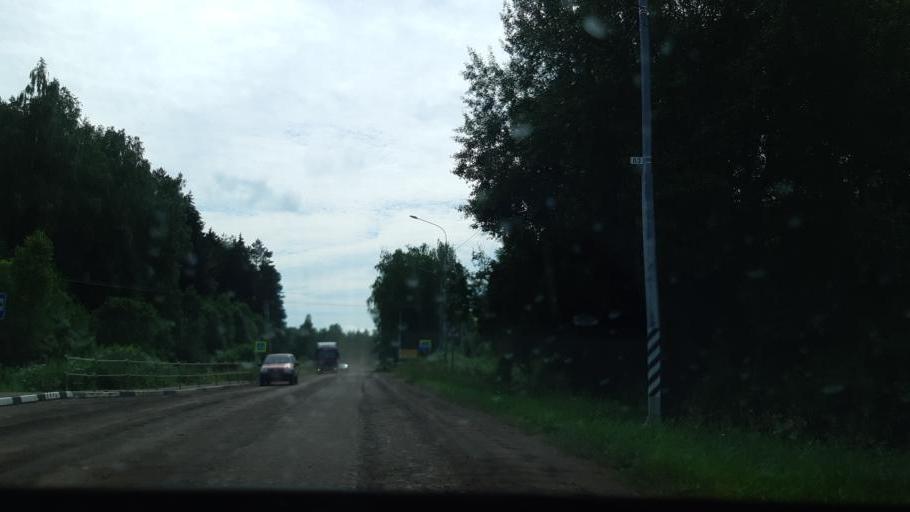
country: RU
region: Moskovskaya
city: Vereya
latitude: 55.3128
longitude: 36.1216
